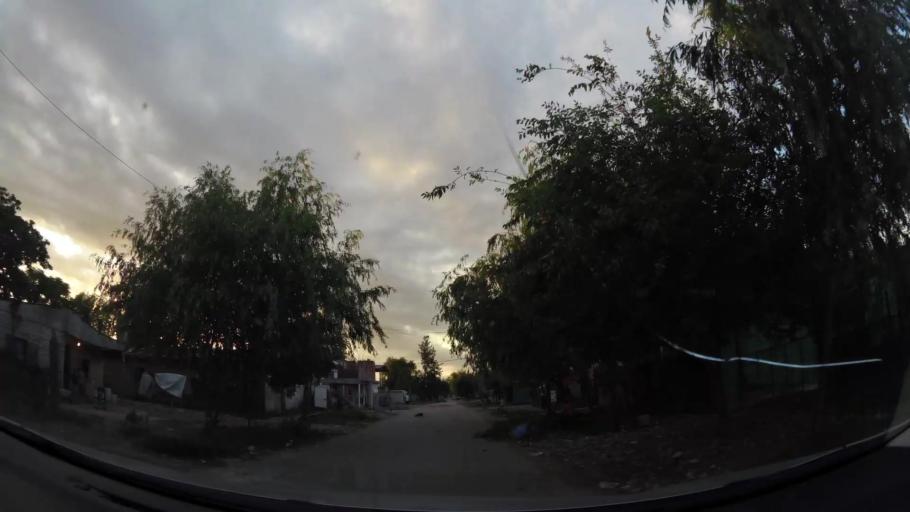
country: AR
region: Buenos Aires
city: Santa Catalina - Dique Lujan
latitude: -34.4393
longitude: -58.6610
